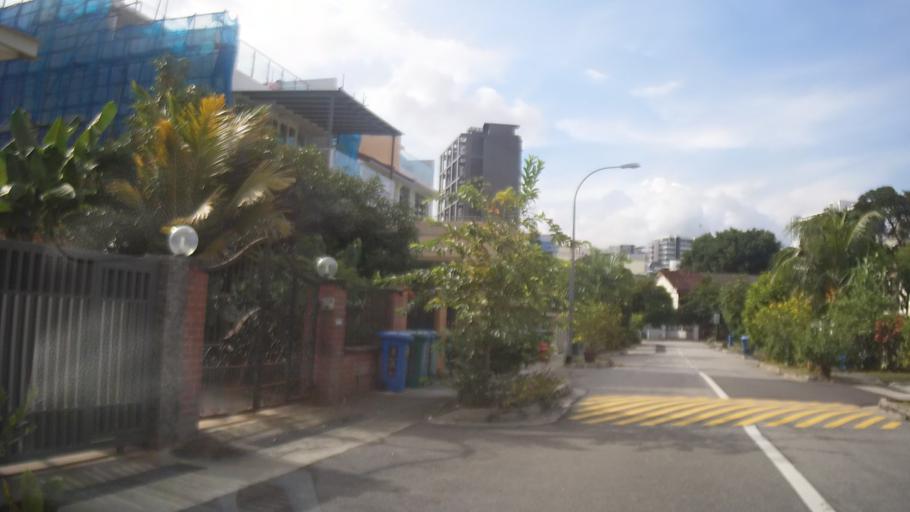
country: SG
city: Singapore
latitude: 1.3308
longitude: 103.8845
